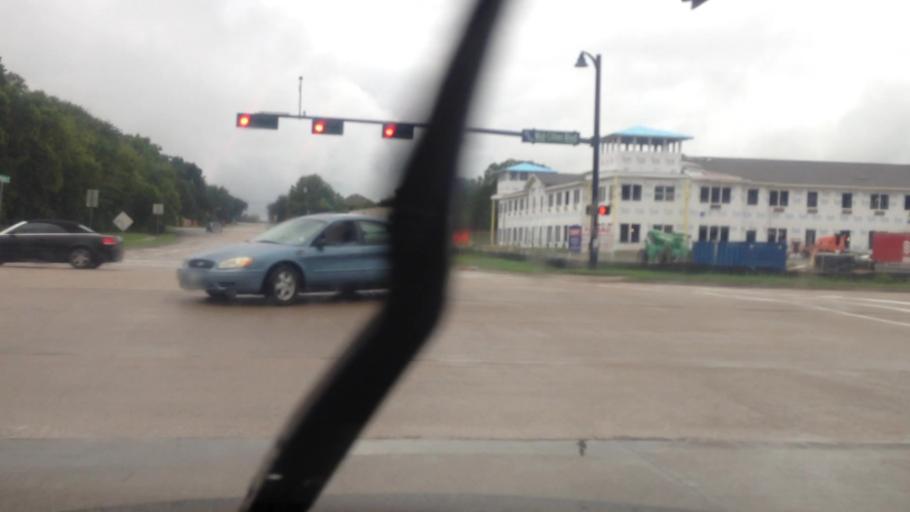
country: US
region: Texas
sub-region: Tarrant County
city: North Richland Hills
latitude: 32.8615
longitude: -97.2032
